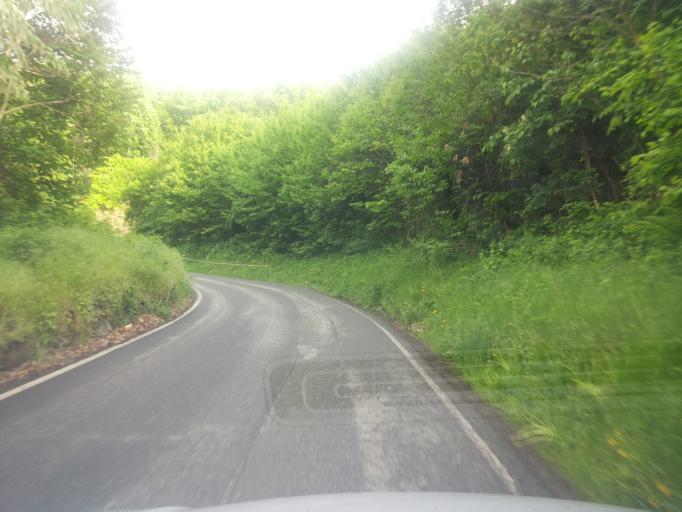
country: IT
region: Piedmont
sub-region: Provincia di Torino
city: Caravino
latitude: 45.3915
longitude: 7.9653
